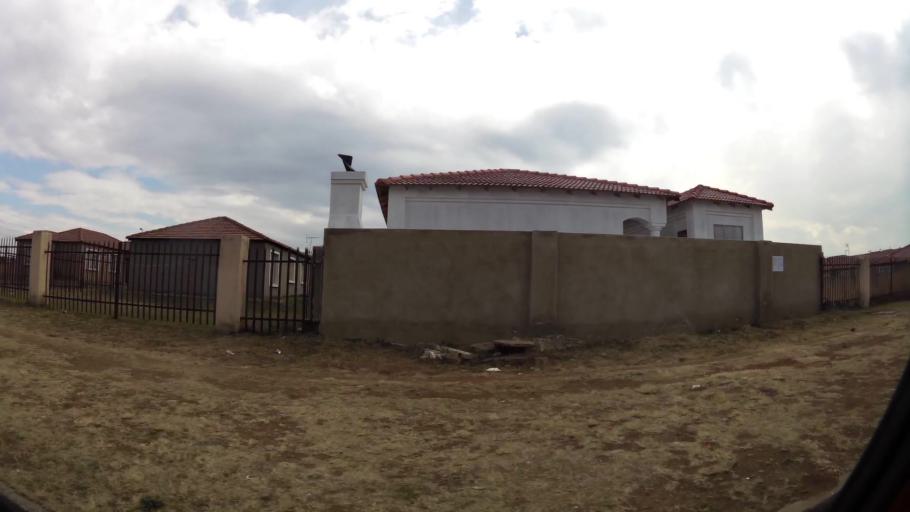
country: ZA
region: Gauteng
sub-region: Sedibeng District Municipality
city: Vanderbijlpark
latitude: -26.7182
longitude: 27.8849
